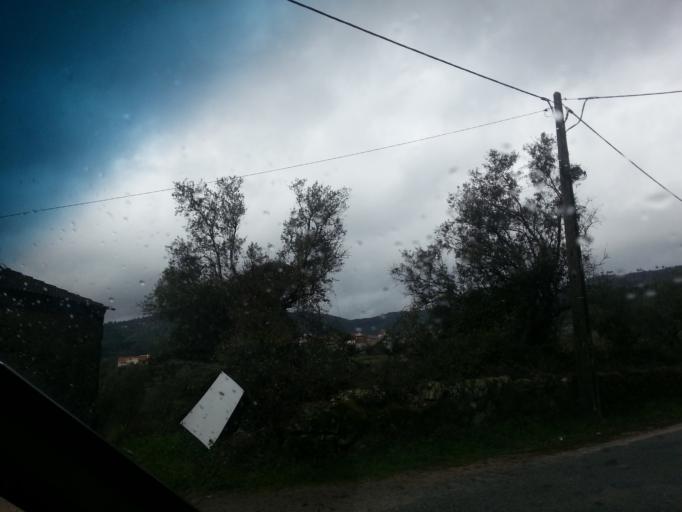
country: PT
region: Guarda
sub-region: Fornos de Algodres
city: Fornos de Algodres
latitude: 40.6137
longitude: -7.5843
